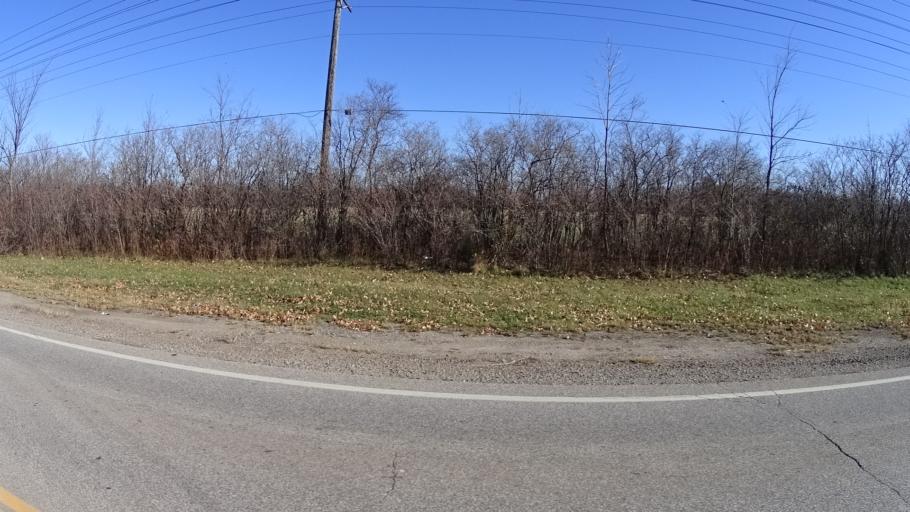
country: US
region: Ohio
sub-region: Lorain County
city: Avon
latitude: 41.4699
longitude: -82.0642
